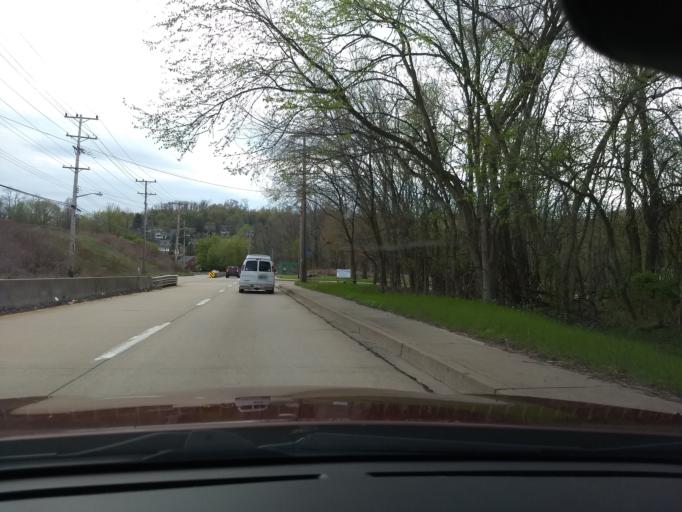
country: US
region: Pennsylvania
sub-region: Allegheny County
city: Wilkinsburg
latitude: 40.4530
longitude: -79.8661
